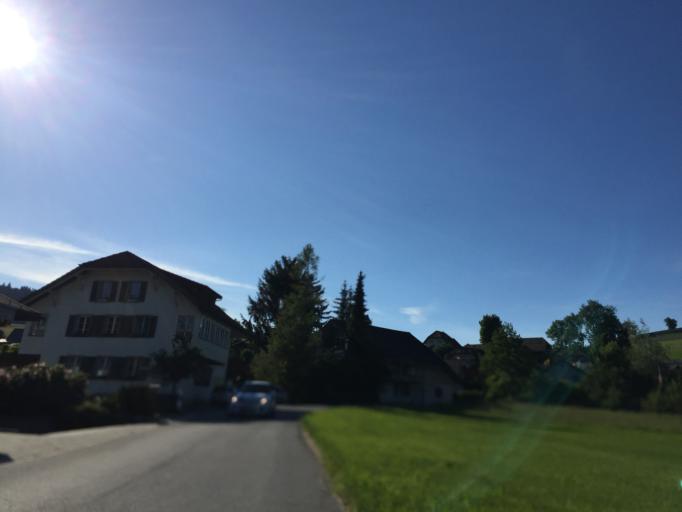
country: CH
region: Bern
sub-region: Bern-Mittelland District
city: Zaziwil
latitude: 46.8940
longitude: 7.6476
